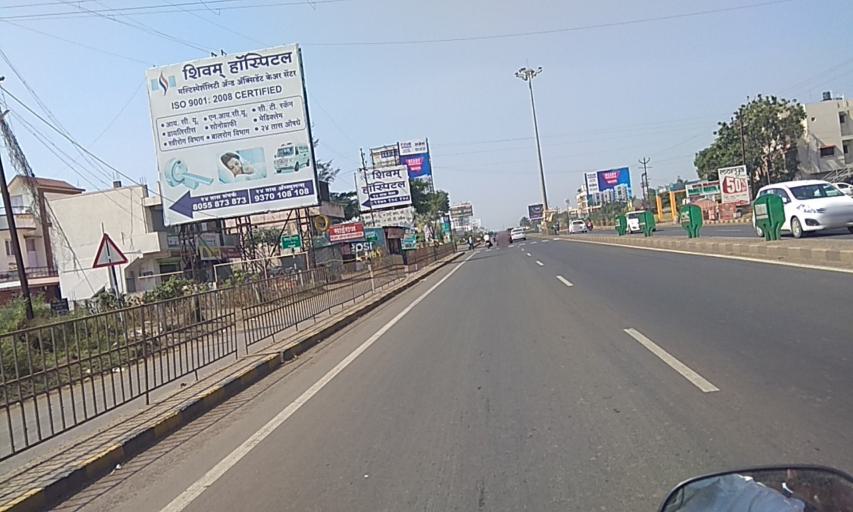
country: IN
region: Maharashtra
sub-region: Pune Division
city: Lohogaon
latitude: 18.4920
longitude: 74.0009
